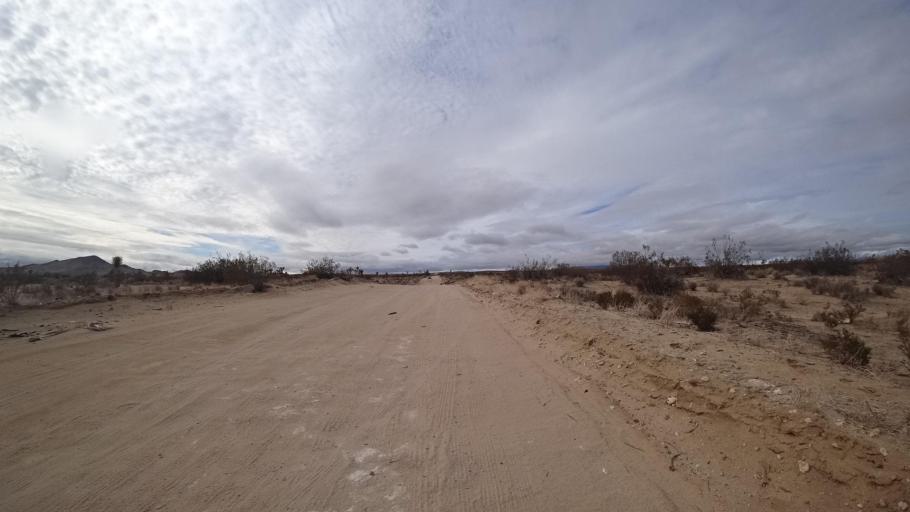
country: US
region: California
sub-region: Kern County
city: Rosamond
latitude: 34.9083
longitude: -118.1541
